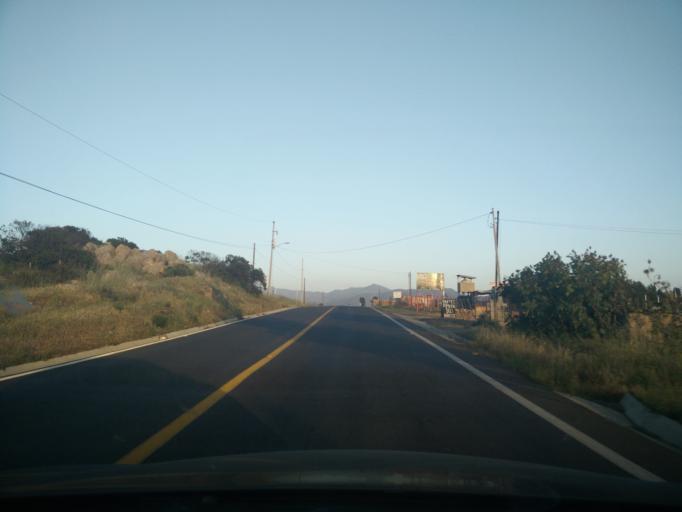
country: MX
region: Baja California
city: El Sauzal
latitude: 32.0068
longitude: -116.6787
